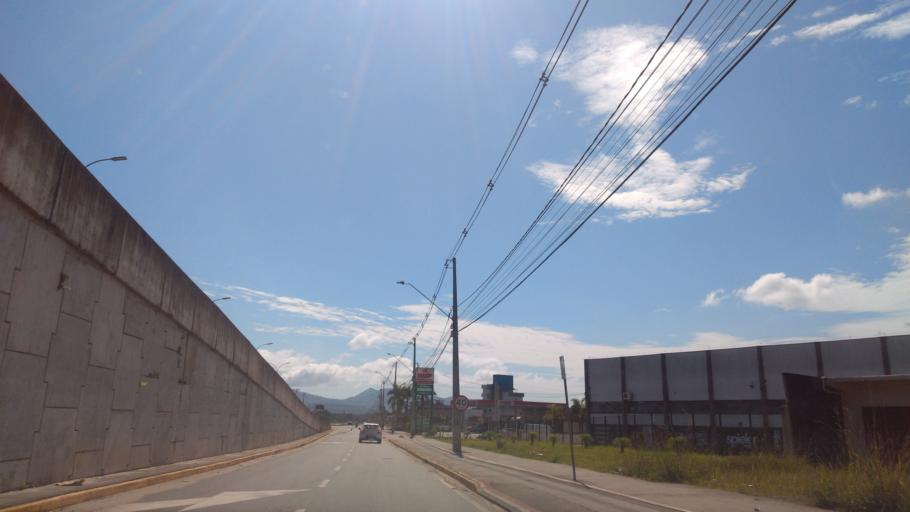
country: BR
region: Santa Catarina
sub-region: Joinville
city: Joinville
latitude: -26.2349
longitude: -48.8170
